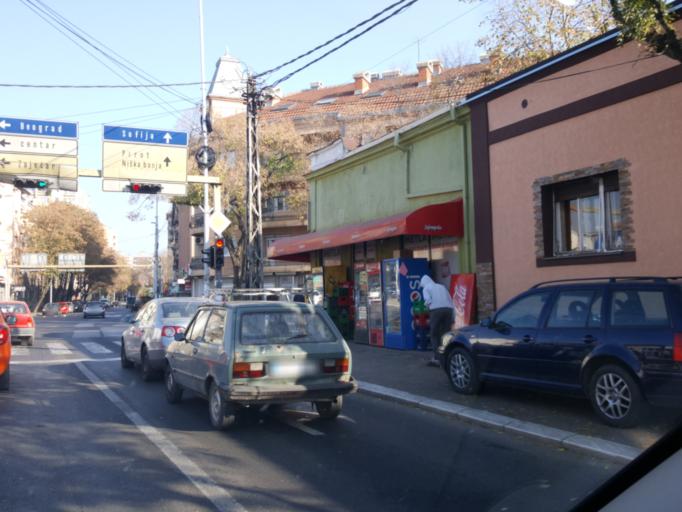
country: RS
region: Central Serbia
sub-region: Nisavski Okrug
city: Nis
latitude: 43.3171
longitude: 21.8861
